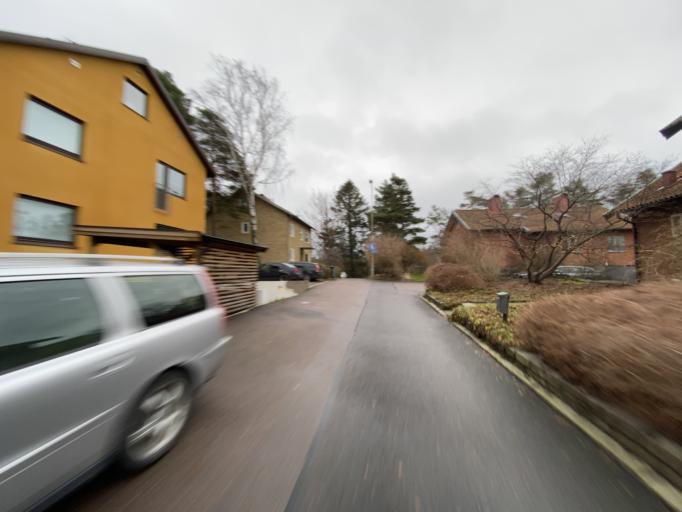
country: SE
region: Vaestra Goetaland
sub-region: Goteborg
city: Eriksbo
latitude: 57.7130
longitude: 12.0460
